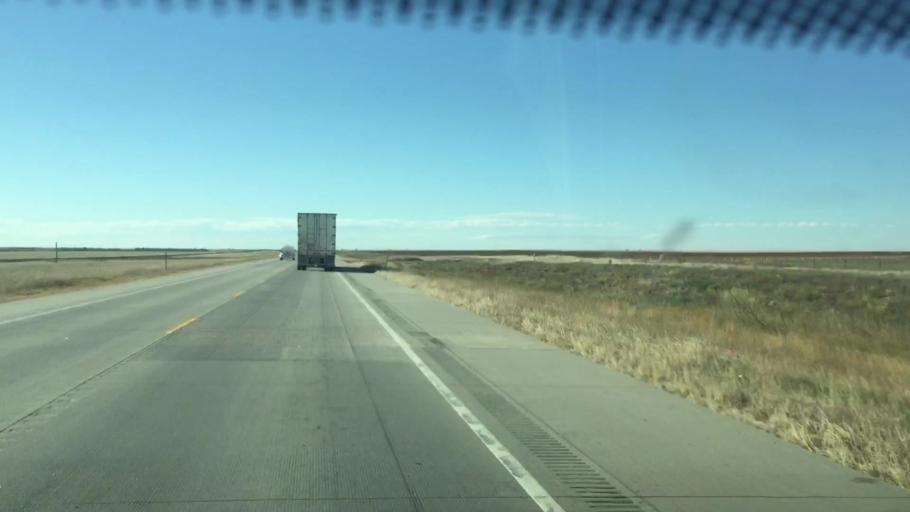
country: US
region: Colorado
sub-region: Kiowa County
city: Eads
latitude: 38.7937
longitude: -102.9413
